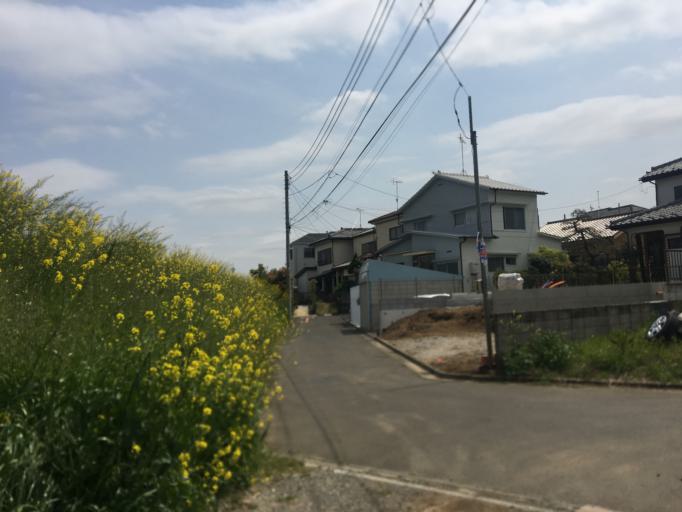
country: JP
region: Saitama
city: Kamifukuoka
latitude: 35.8805
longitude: 139.5291
